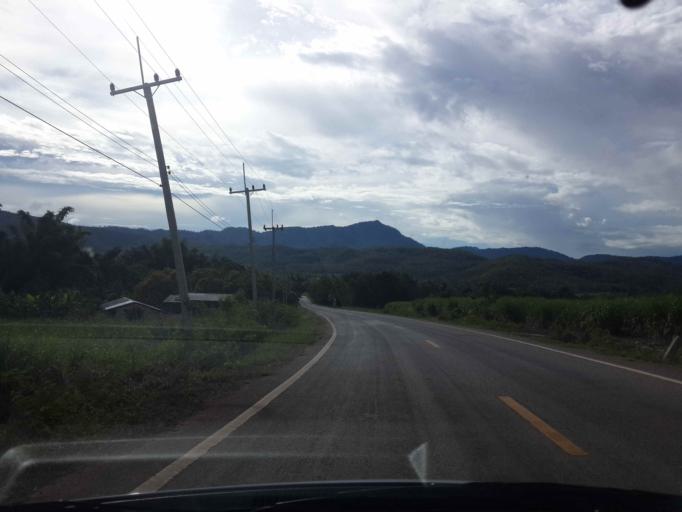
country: TH
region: Kanchanaburi
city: Dan Makham Tia
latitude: 13.8189
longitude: 99.1810
